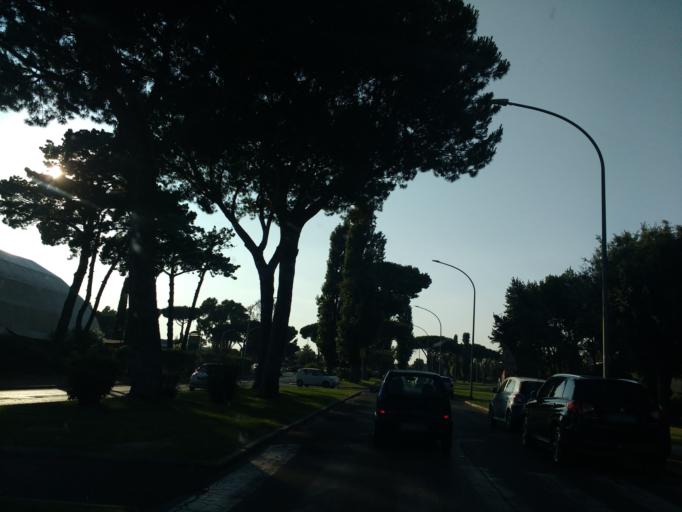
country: IT
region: Latium
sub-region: Citta metropolitana di Roma Capitale
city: Acilia-Castel Fusano-Ostia Antica
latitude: 41.7510
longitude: 12.3517
